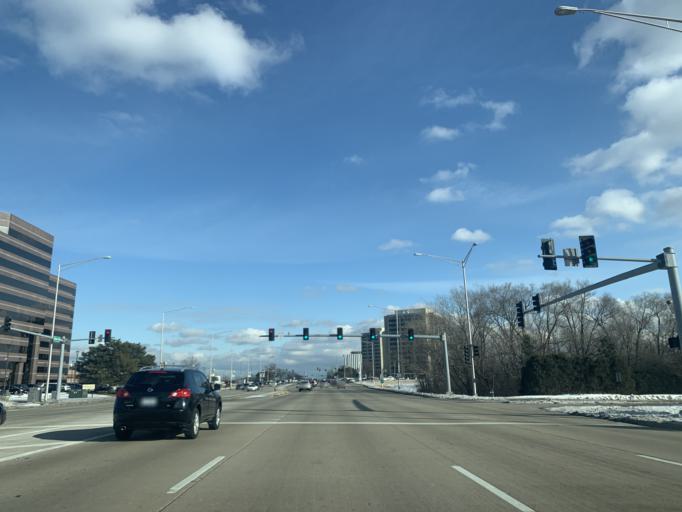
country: US
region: Illinois
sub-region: DuPage County
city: Oakbrook Terrace
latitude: 41.8464
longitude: -87.9624
